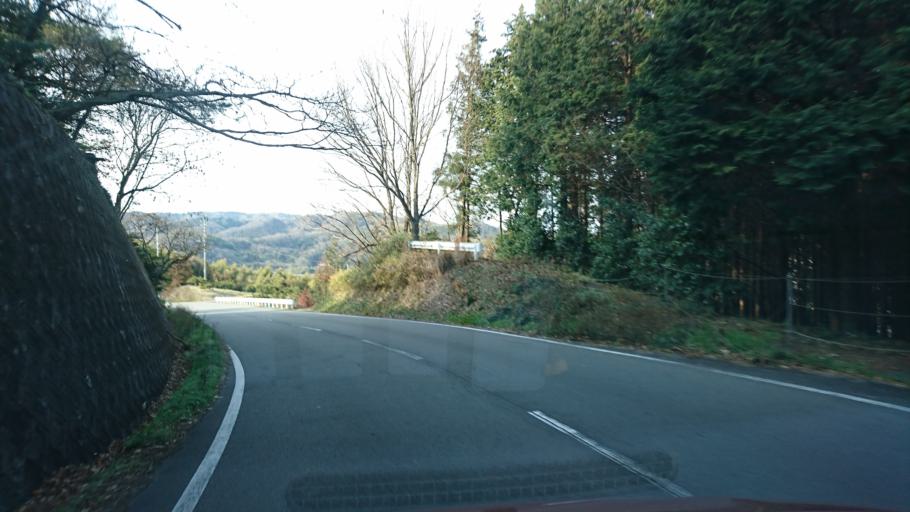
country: JP
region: Ehime
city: Hojo
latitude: 34.0232
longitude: 132.9662
